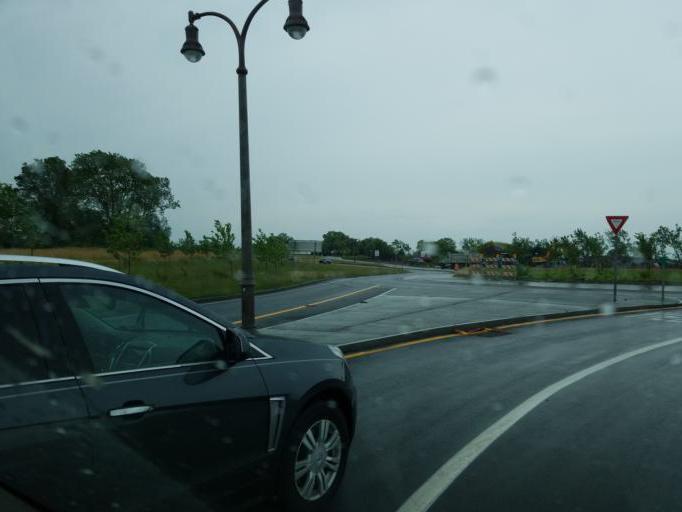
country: US
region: New York
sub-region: Niagara County
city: Niagara Falls
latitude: 43.0814
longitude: -79.0513
